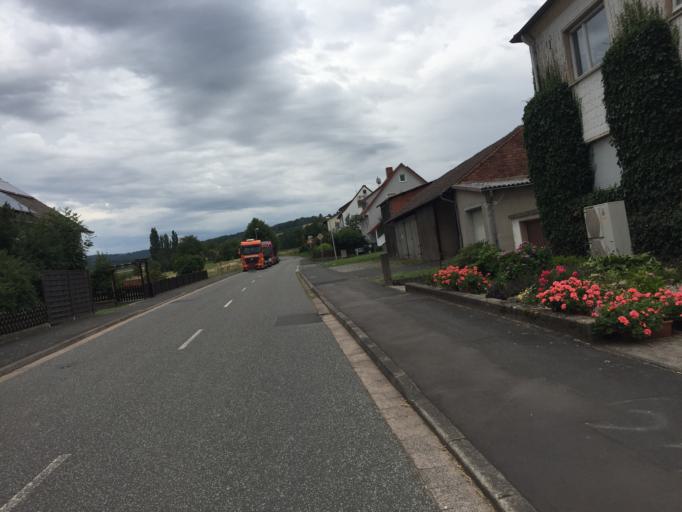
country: DE
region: Hesse
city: Breitenbach
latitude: 50.9184
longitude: 9.7648
